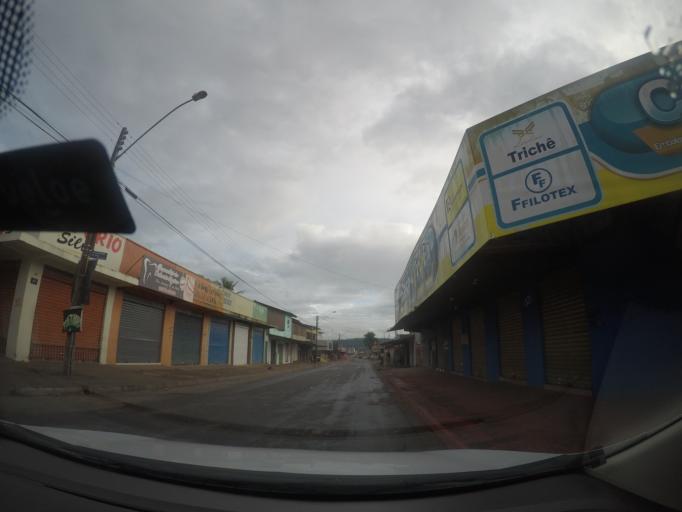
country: BR
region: Goias
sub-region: Goiania
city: Goiania
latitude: -16.7008
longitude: -49.3525
